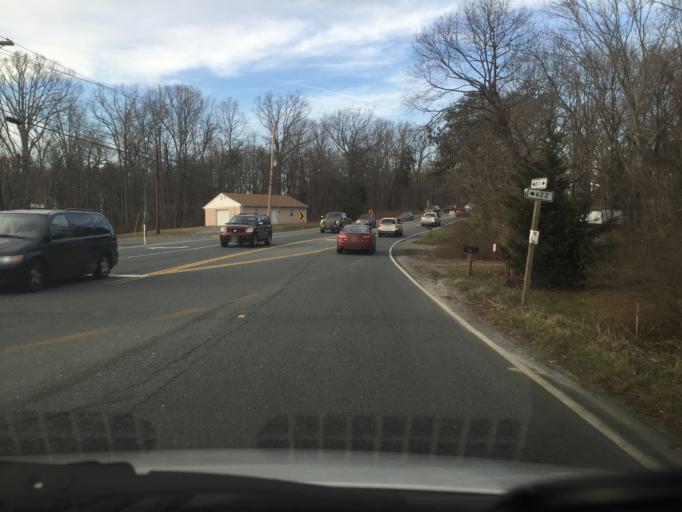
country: US
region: Virginia
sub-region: Bedford County
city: Forest
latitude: 37.3500
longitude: -79.2827
